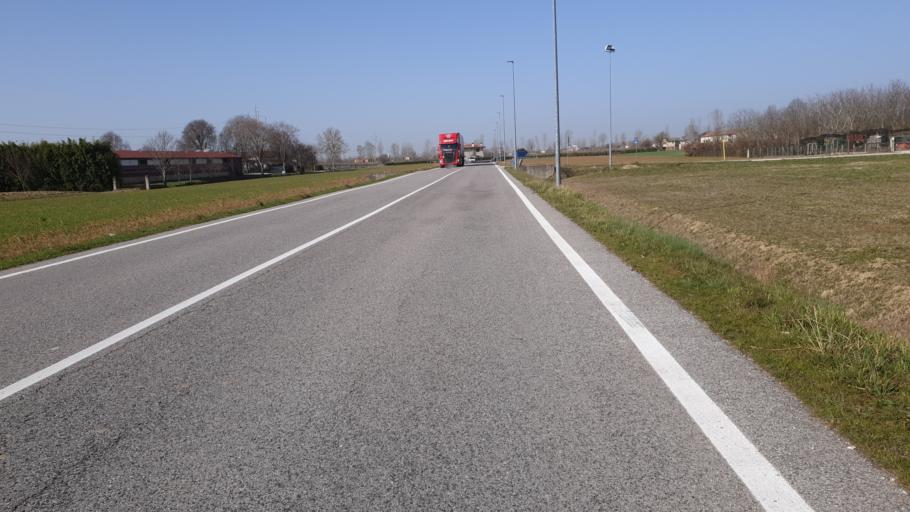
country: IT
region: Veneto
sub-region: Provincia di Padova
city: Cavino
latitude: 45.4957
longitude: 11.8898
